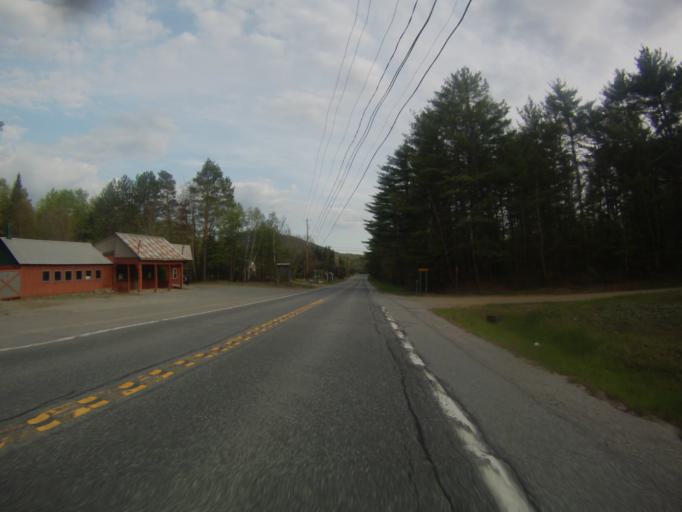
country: US
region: New York
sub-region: Warren County
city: Warrensburg
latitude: 43.6444
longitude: -73.9494
